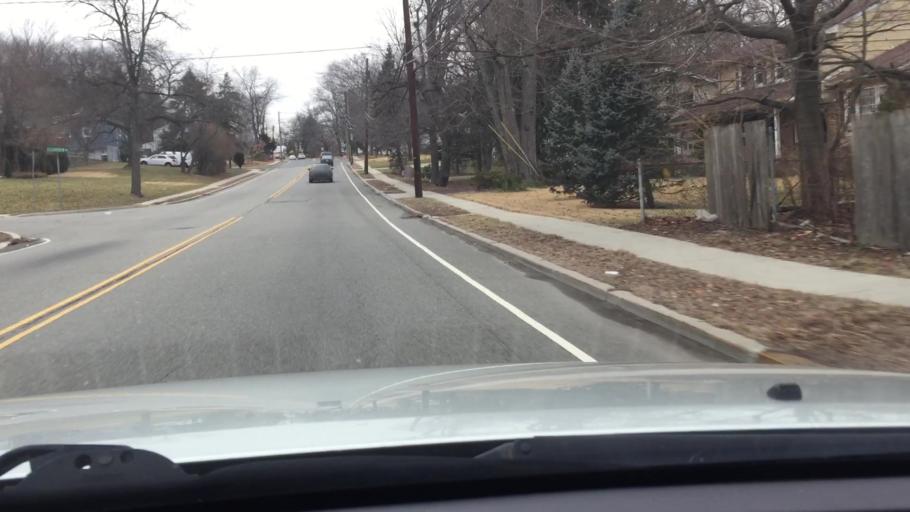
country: US
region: New Jersey
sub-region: Middlesex County
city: Old Bridge
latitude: 40.4151
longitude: -74.3881
